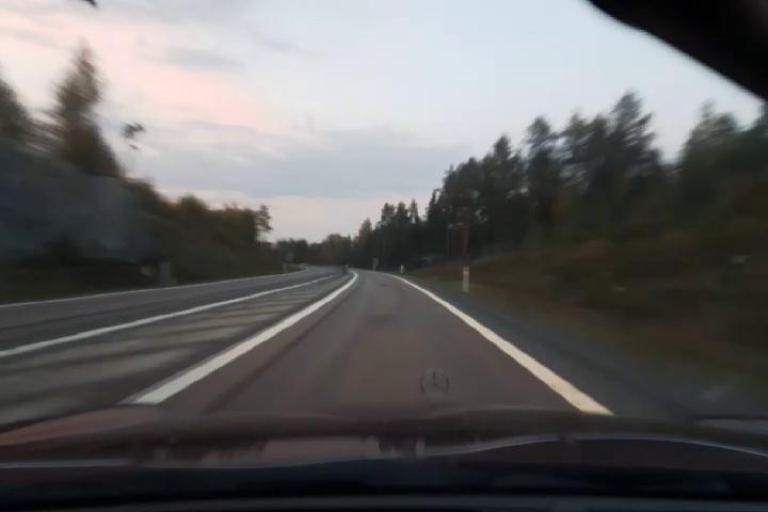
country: SE
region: Vaesternorrland
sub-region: Kramfors Kommun
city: Nordingra
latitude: 62.8853
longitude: 18.0863
